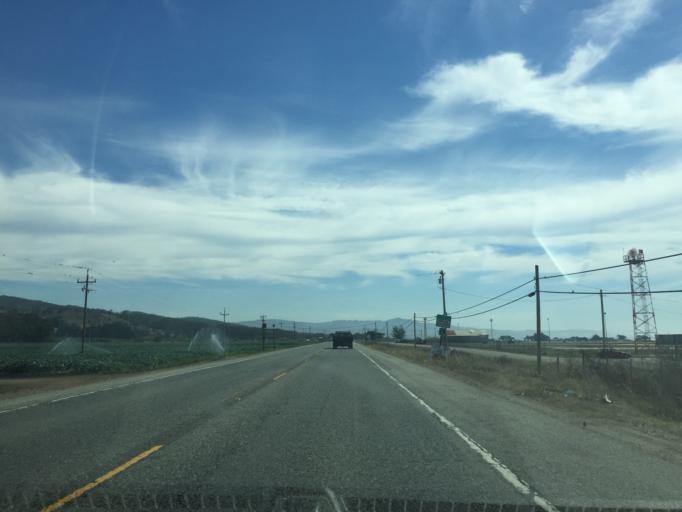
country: US
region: California
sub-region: San Mateo County
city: Moss Beach
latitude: 37.5170
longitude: -122.4991
